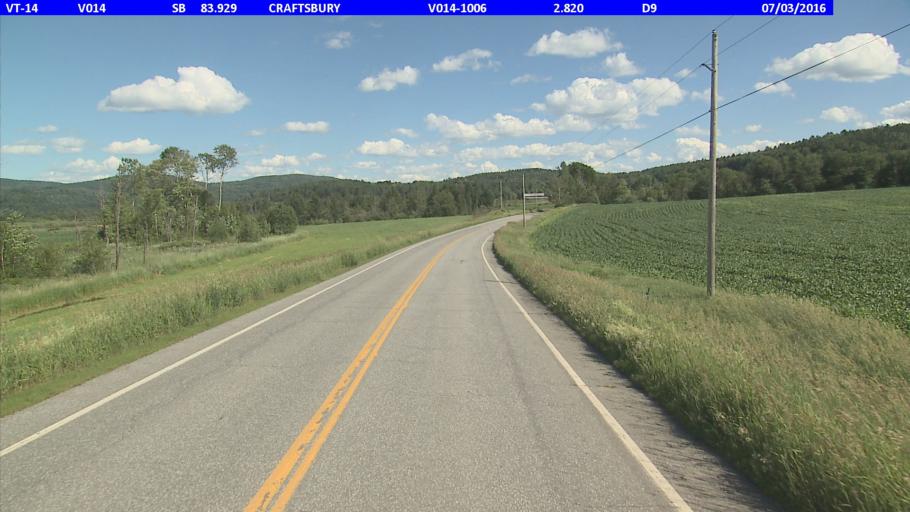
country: US
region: Vermont
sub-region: Caledonia County
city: Hardwick
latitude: 44.6334
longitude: -72.3939
